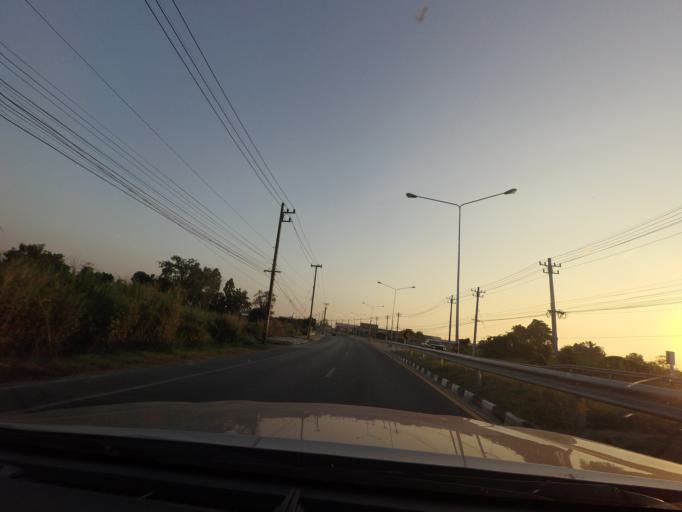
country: TH
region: Sukhothai
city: Si Samrong
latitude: 17.0952
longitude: 99.8367
